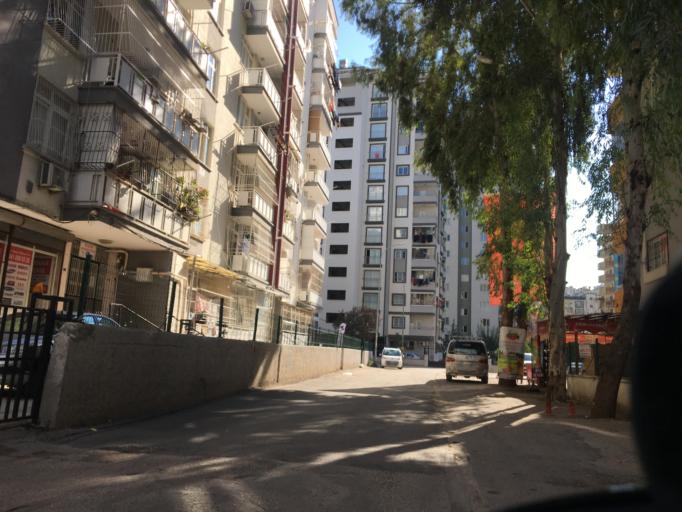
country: TR
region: Adana
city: Seyhan
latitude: 37.0228
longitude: 35.2862
